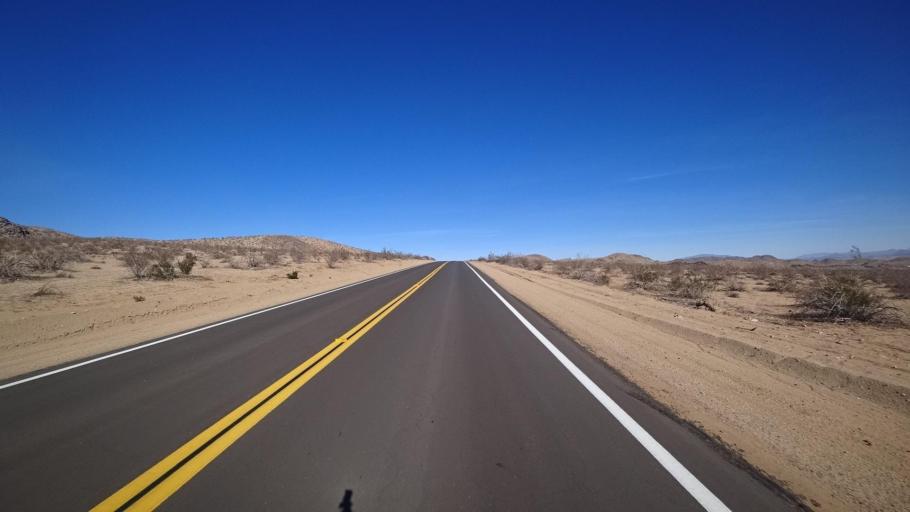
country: US
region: California
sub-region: Kern County
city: Ridgecrest
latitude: 35.5360
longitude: -117.5880
